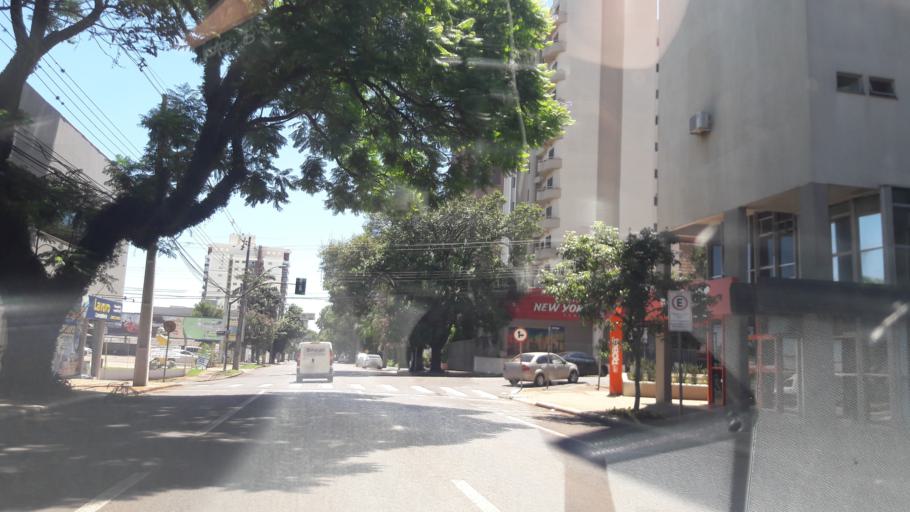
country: BR
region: Parana
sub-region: Cascavel
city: Cascavel
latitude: -24.9523
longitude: -53.4564
